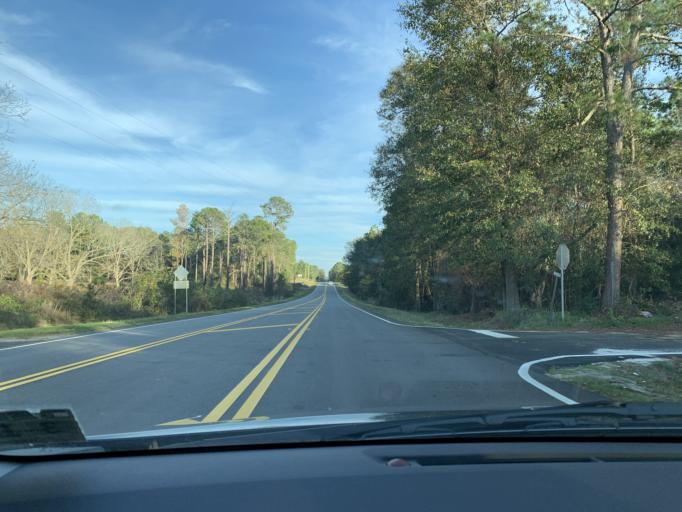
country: US
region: Georgia
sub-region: Irwin County
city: Ocilla
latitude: 31.5958
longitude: -83.1492
